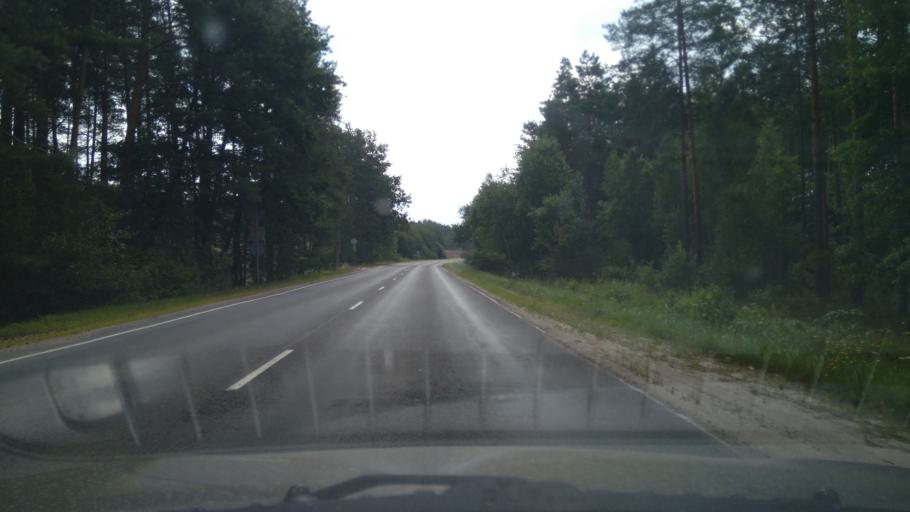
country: BY
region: Brest
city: Nyakhachava
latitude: 52.5868
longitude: 25.0954
